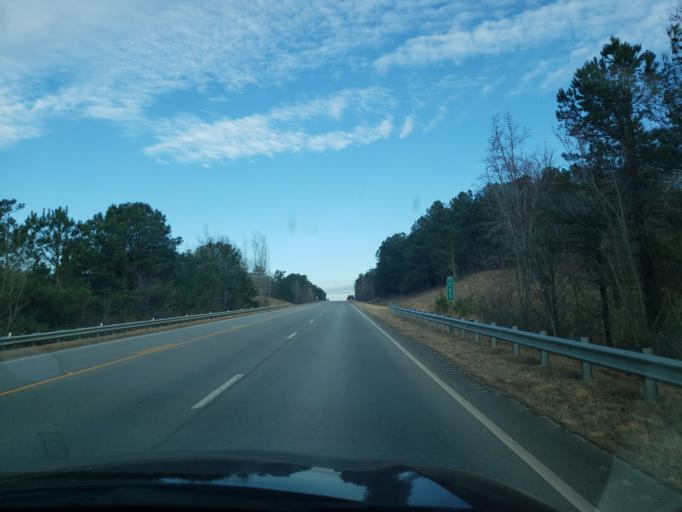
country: US
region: Alabama
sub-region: Randolph County
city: Wedowee
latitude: 33.4403
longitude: -85.5630
